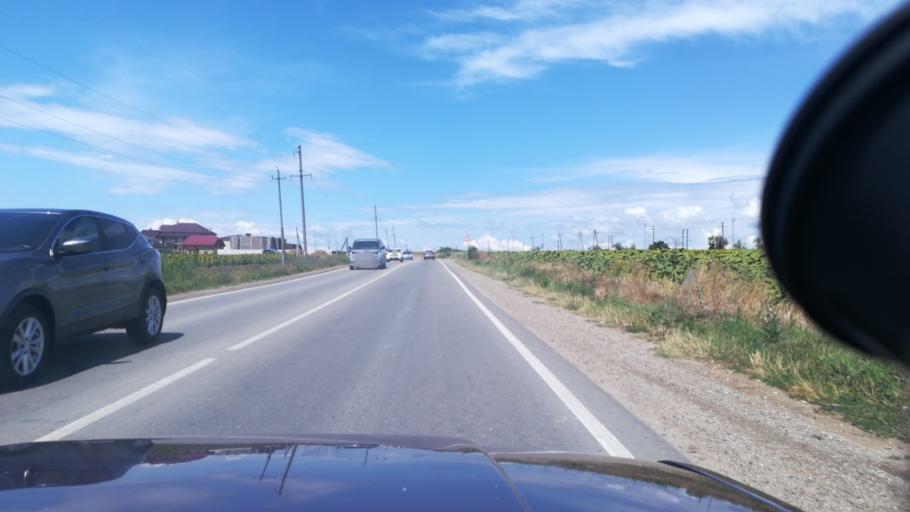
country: RU
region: Krasnodarskiy
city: Tsibanobalka
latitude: 44.9610
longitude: 37.3041
